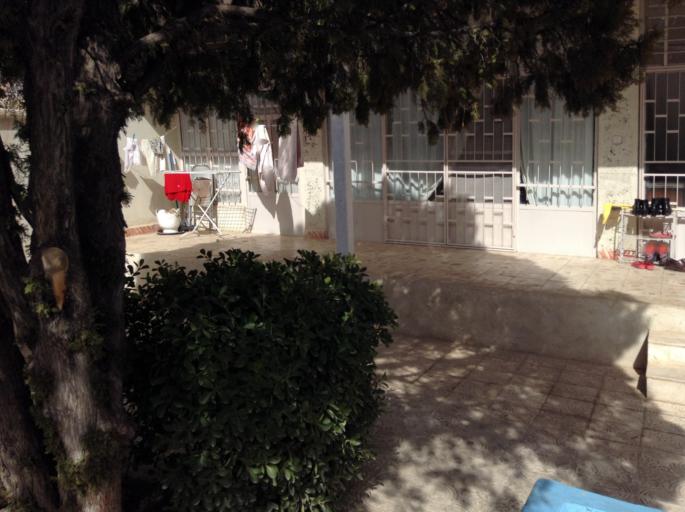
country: IR
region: Markazi
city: Khomeyn
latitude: 33.6461
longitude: 50.0781
